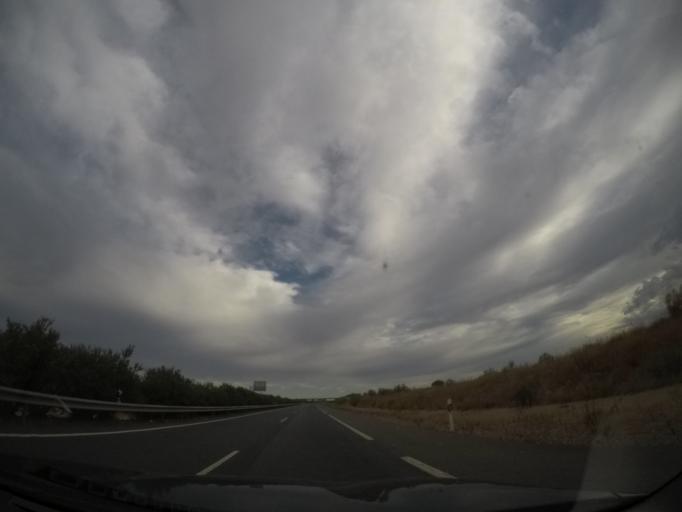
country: ES
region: Andalusia
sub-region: Provincia de Huelva
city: Huelva
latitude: 37.3288
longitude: -6.9138
